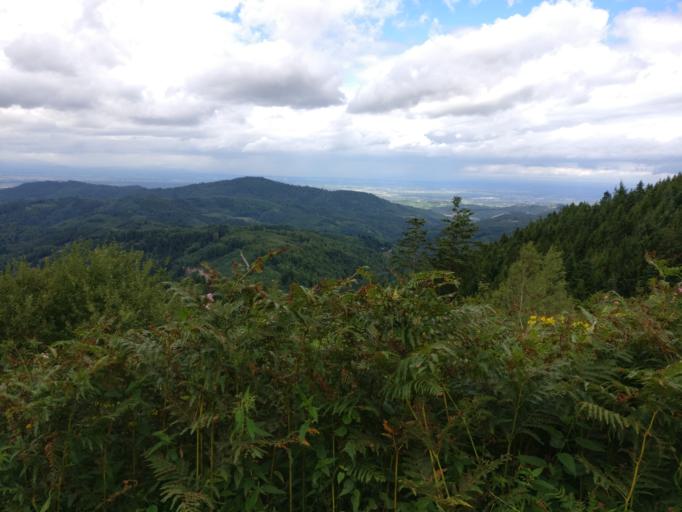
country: DE
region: Baden-Wuerttemberg
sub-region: Freiburg Region
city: Nordrach
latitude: 48.4492
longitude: 8.0919
